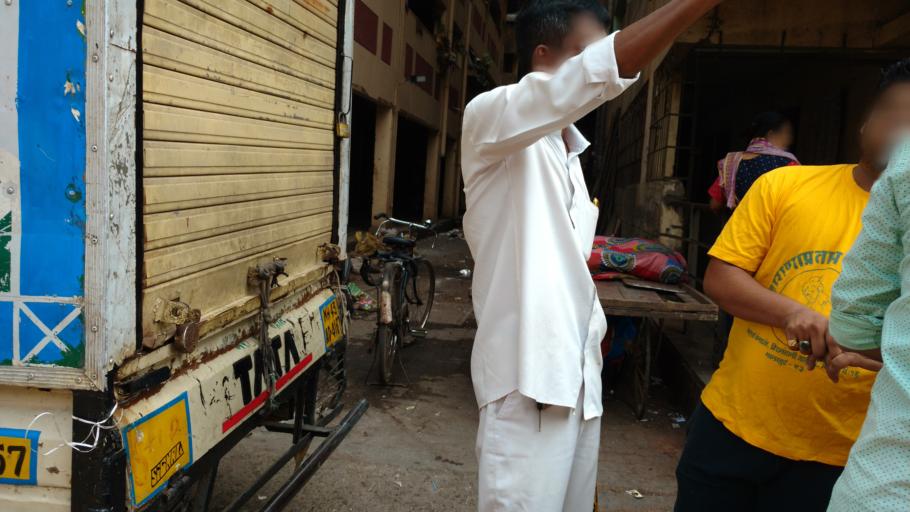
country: IN
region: Maharashtra
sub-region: Mumbai Suburban
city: Mumbai
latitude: 19.0643
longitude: 72.9156
